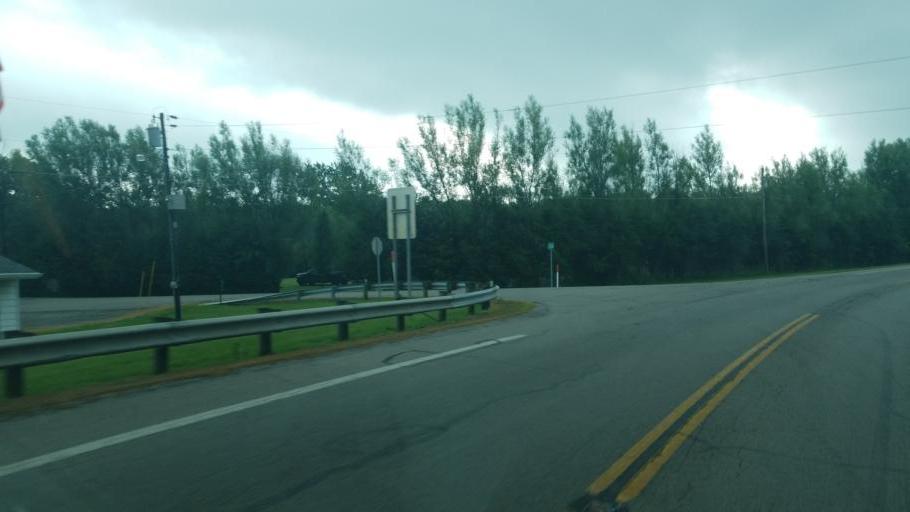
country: US
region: Ohio
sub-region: Logan County
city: Russells Point
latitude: 40.5569
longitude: -83.8343
